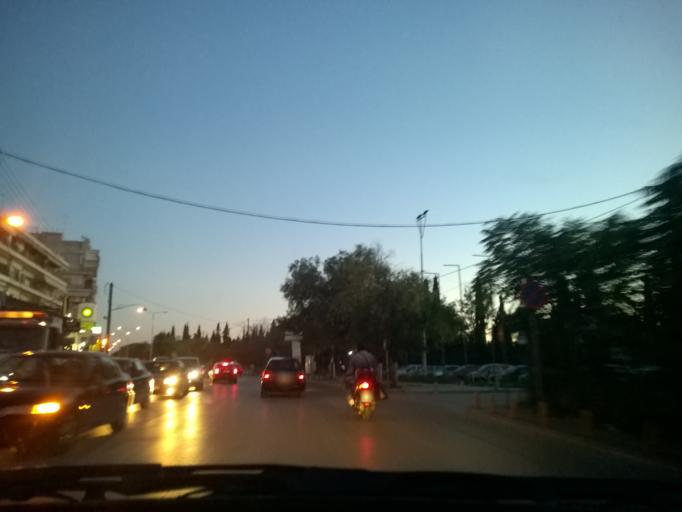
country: GR
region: Central Macedonia
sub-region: Nomos Thessalonikis
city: Ampelokipoi
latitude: 40.6565
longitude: 22.9344
